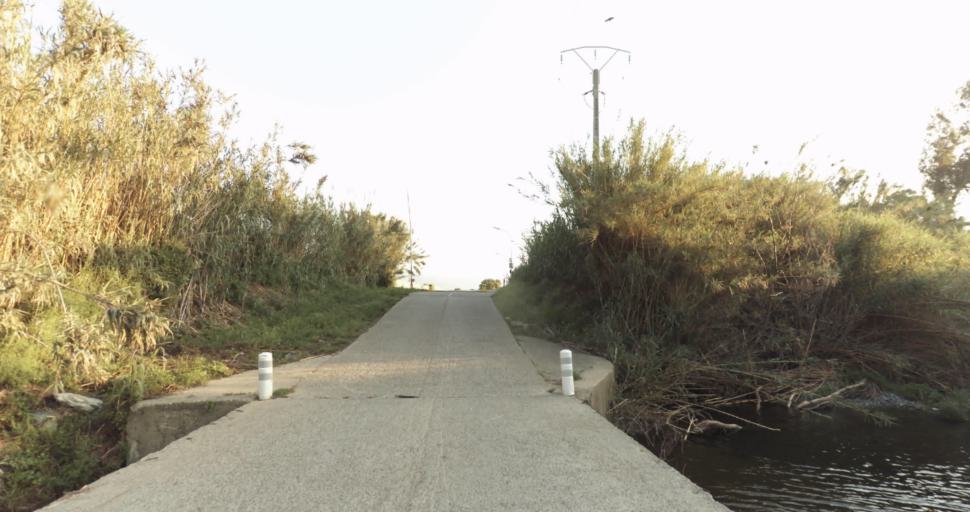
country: FR
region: Corsica
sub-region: Departement de la Haute-Corse
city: Biguglia
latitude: 42.6162
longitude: 9.4434
